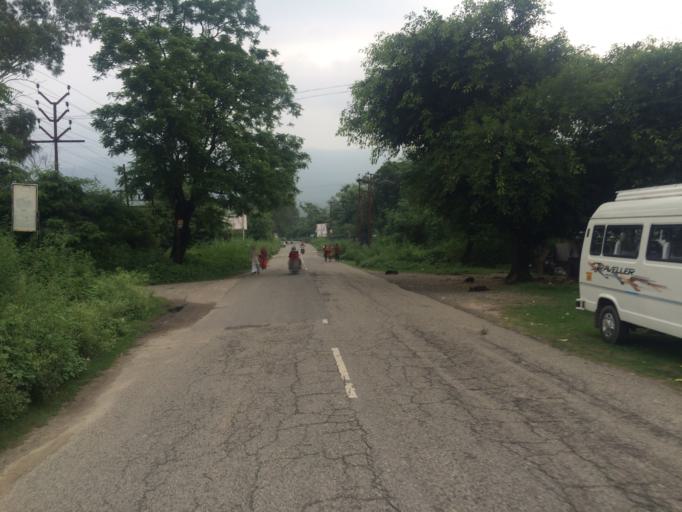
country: IN
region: Uttarakhand
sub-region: Dehradun
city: Birbhaddar
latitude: 30.0731
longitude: 78.2814
